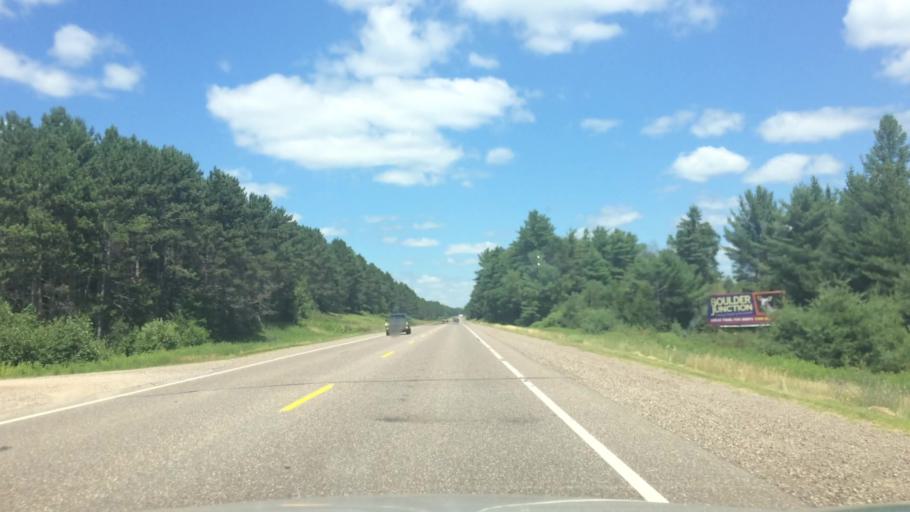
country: US
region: Wisconsin
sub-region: Vilas County
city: Lac du Flambeau
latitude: 45.9583
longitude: -89.7004
